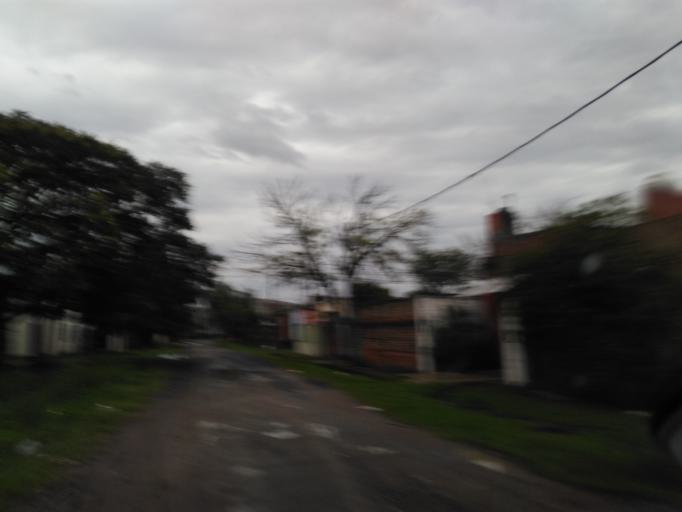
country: AR
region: Chaco
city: Resistencia
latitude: -27.4675
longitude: -58.9802
